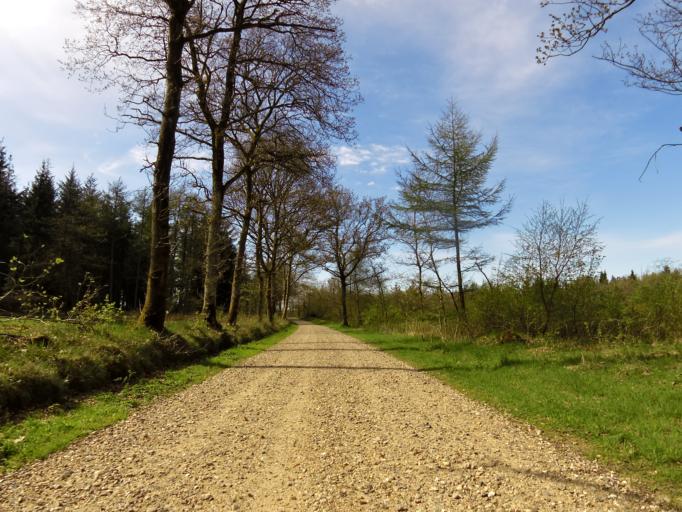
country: DK
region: Central Jutland
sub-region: Holstebro Kommune
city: Vinderup
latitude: 56.4760
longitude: 8.8765
